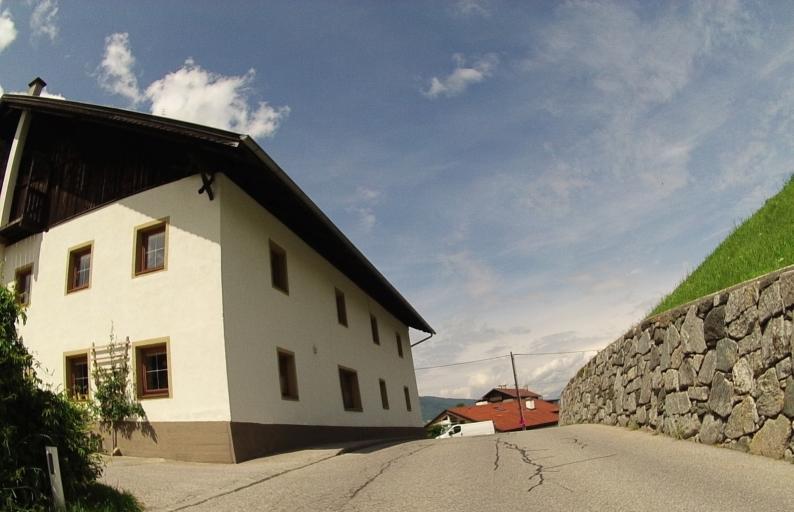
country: AT
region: Tyrol
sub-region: Politischer Bezirk Innsbruck Land
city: Ellbogen
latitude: 47.1808
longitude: 11.4363
